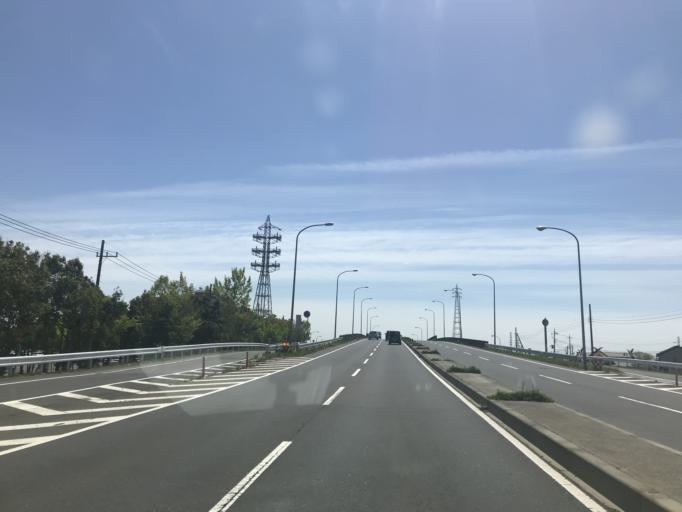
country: JP
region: Ibaraki
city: Ishige
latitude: 36.1897
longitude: 139.9881
